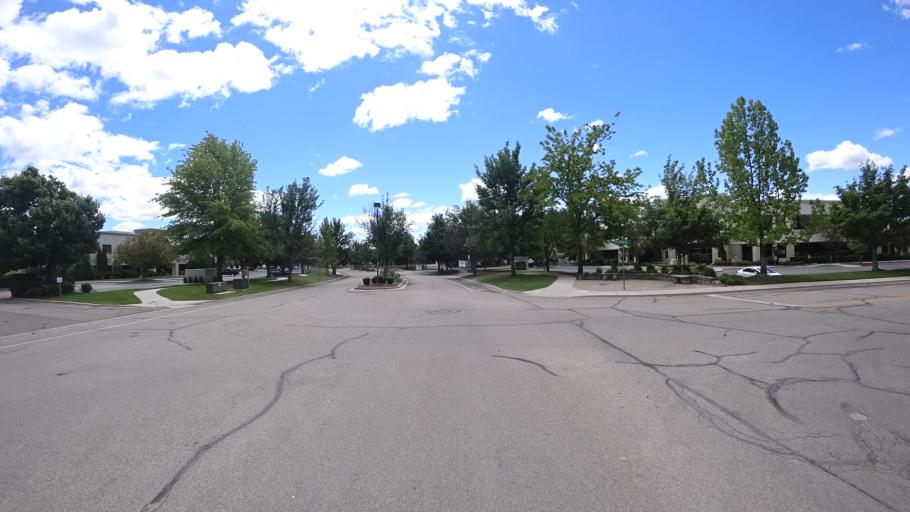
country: US
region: Idaho
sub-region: Ada County
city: Eagle
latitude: 43.6620
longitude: -116.3393
